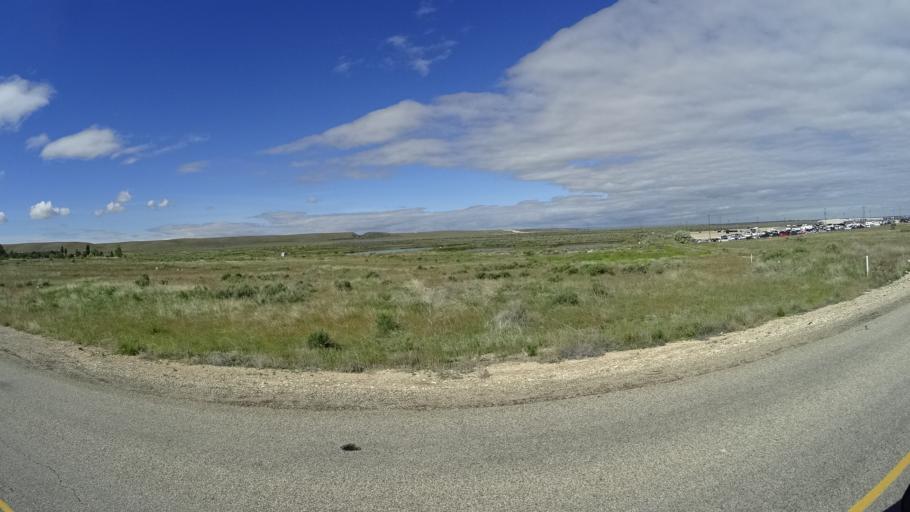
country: US
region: Idaho
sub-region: Ada County
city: Boise
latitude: 43.5312
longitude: -116.1579
